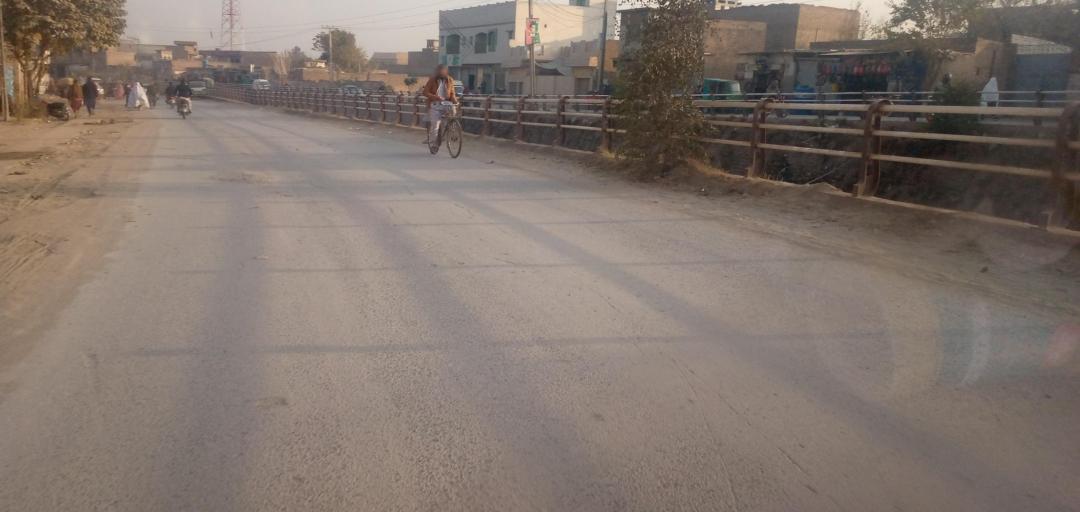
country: PK
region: Khyber Pakhtunkhwa
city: Peshawar
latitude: 33.9735
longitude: 71.5198
